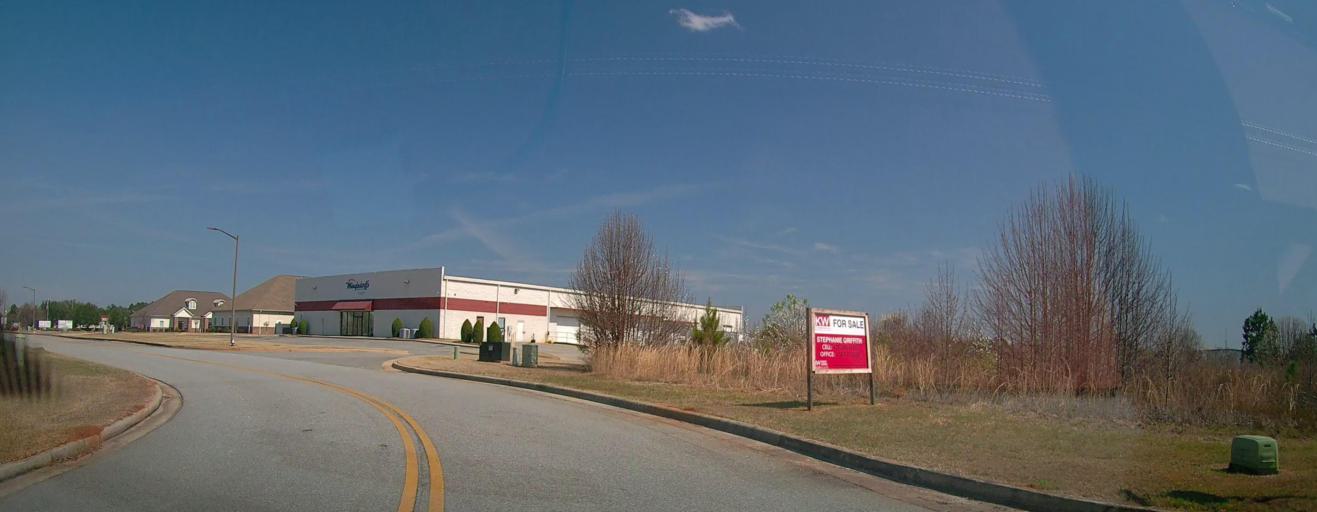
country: US
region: Georgia
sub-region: Houston County
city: Centerville
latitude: 32.6108
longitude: -83.6842
